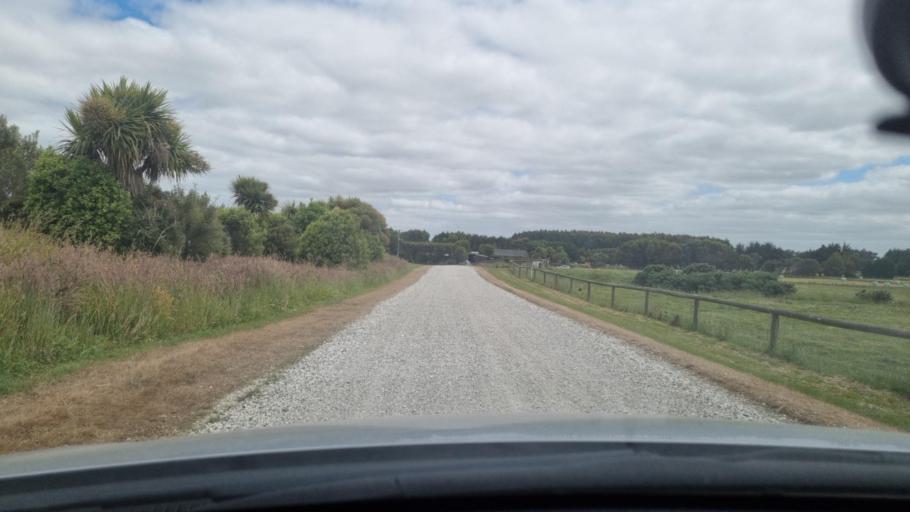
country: NZ
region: Southland
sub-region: Invercargill City
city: Invercargill
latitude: -46.4220
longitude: 168.2927
